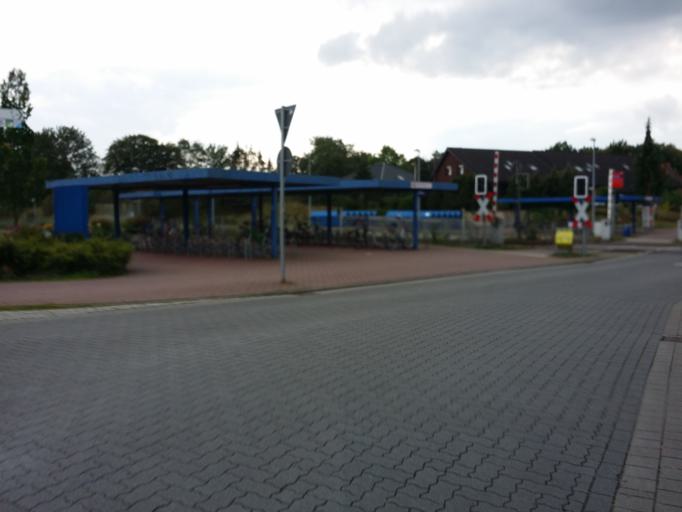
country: DE
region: Lower Saxony
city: Hemmoor
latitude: 53.6841
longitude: 9.1664
